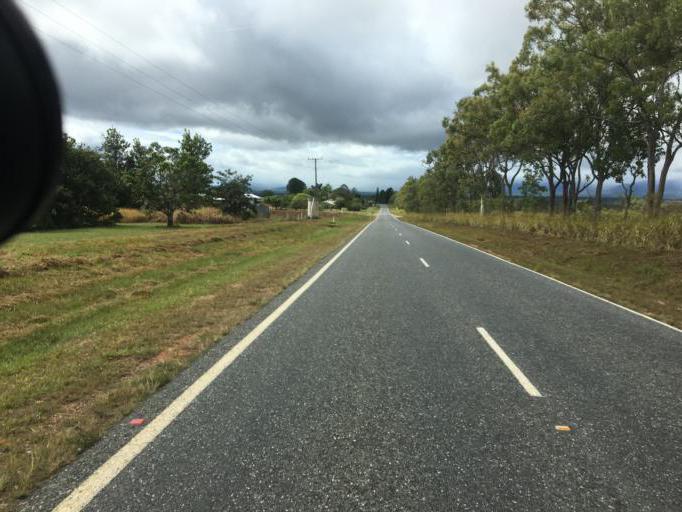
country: AU
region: Queensland
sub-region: Tablelands
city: Mareeba
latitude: -17.0160
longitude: 145.3557
